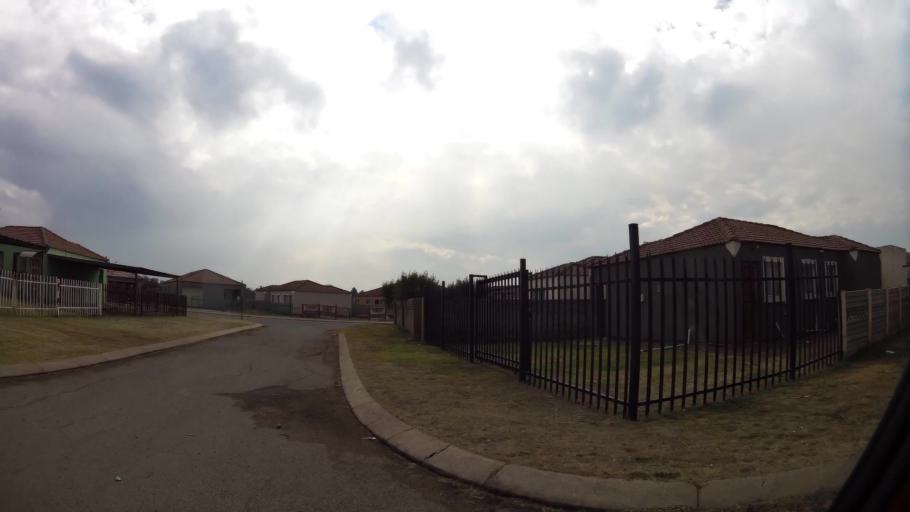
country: ZA
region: Gauteng
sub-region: Sedibeng District Municipality
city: Vanderbijlpark
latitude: -26.7151
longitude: 27.8849
